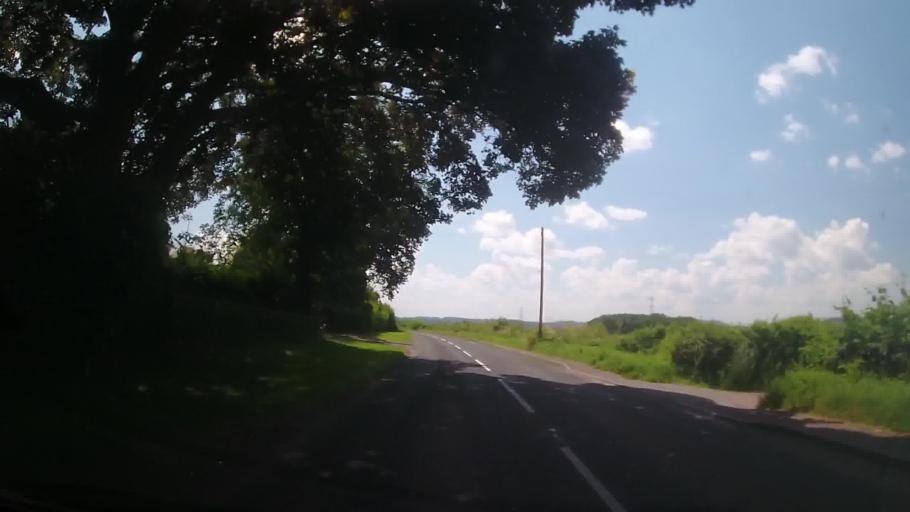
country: GB
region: England
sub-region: Herefordshire
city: Withington
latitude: 52.0437
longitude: -2.6254
